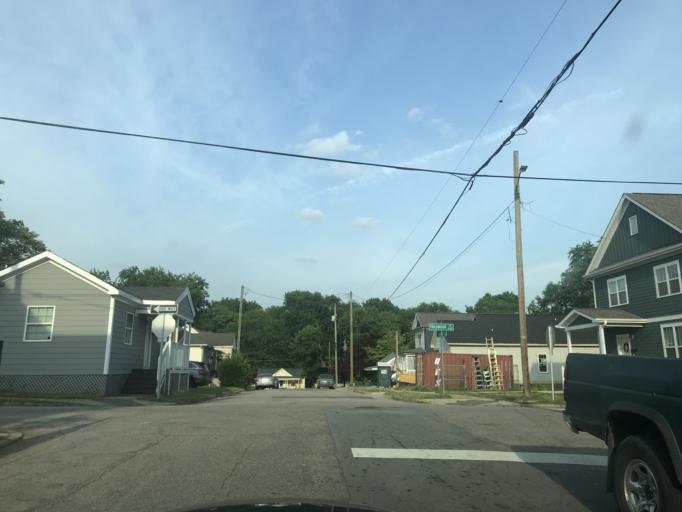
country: US
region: North Carolina
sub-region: Wake County
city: Raleigh
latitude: 35.7740
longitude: -78.6284
